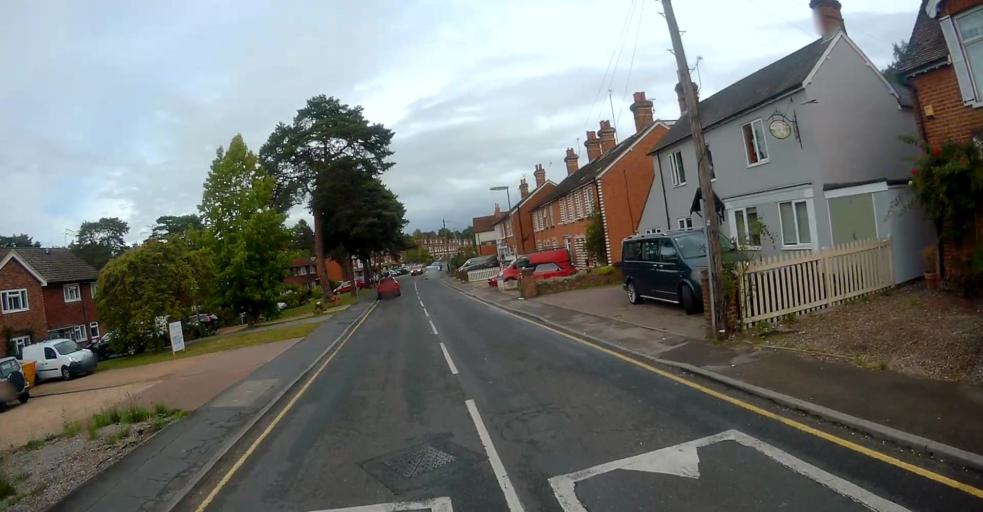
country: GB
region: England
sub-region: Surrey
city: Pirbright
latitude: 51.3036
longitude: -0.6457
